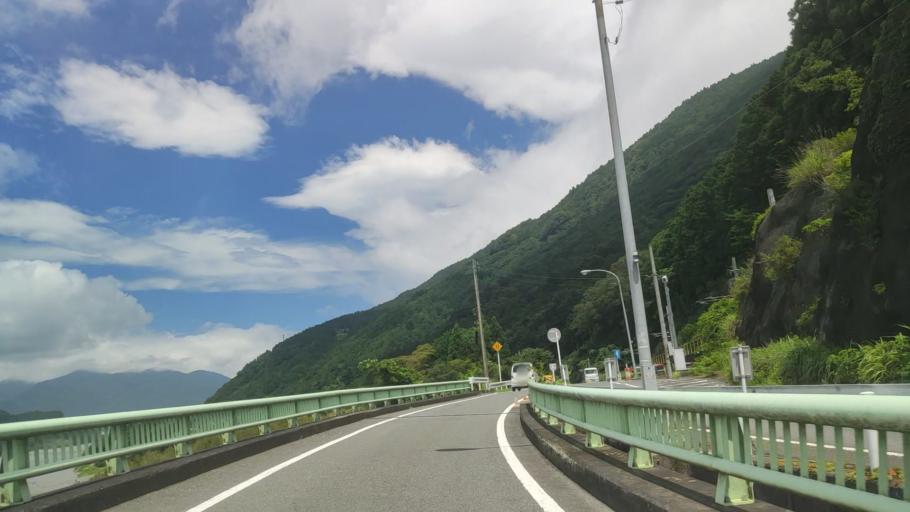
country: JP
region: Shizuoka
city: Fujinomiya
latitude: 35.2584
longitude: 138.4800
